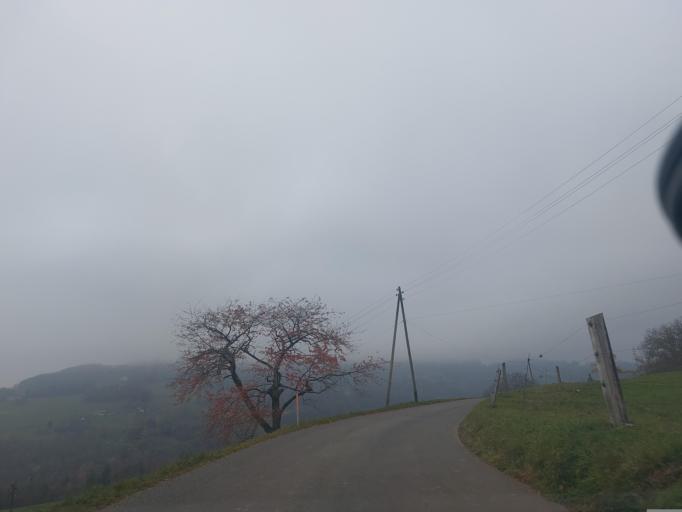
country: CH
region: Vaud
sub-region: Riviera-Pays-d'Enhaut District
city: Blonay
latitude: 46.4817
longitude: 6.8828
